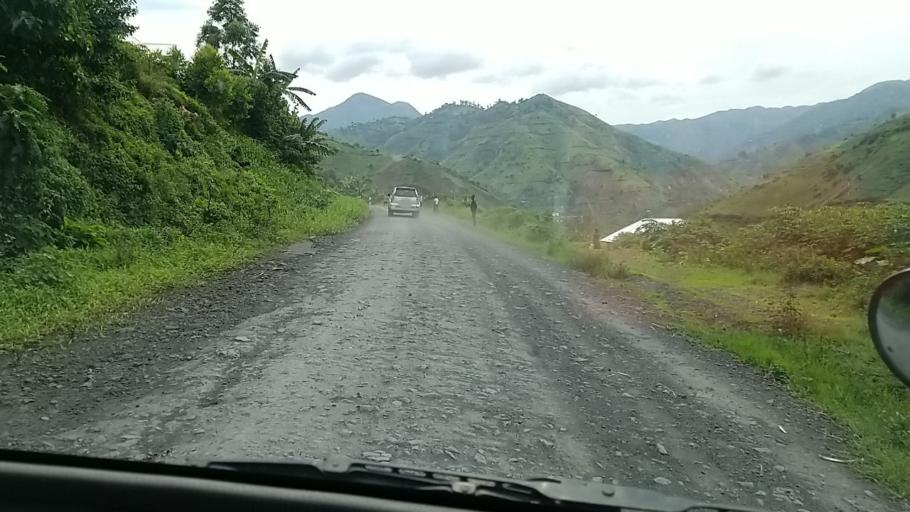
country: CD
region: Nord Kivu
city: Sake
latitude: -1.7402
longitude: 28.9983
